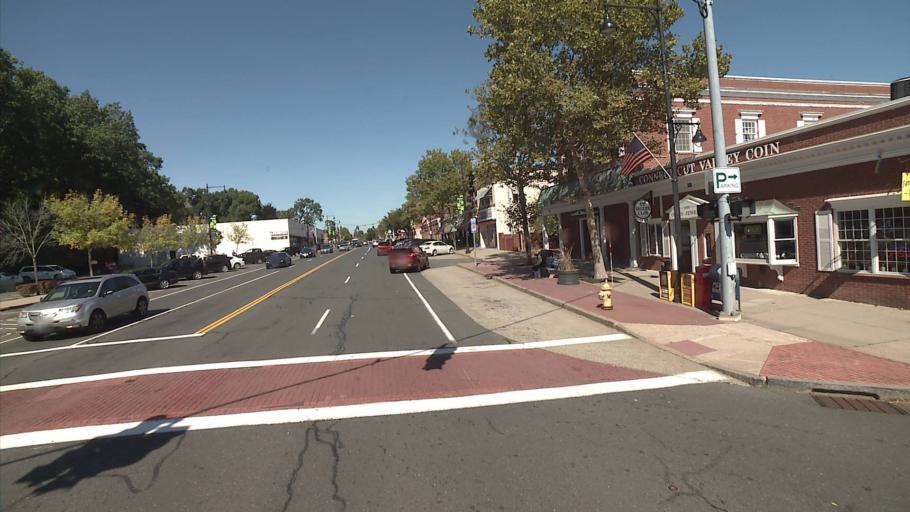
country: US
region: Connecticut
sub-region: Hartford County
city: Manchester
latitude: 41.7680
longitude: -72.5205
